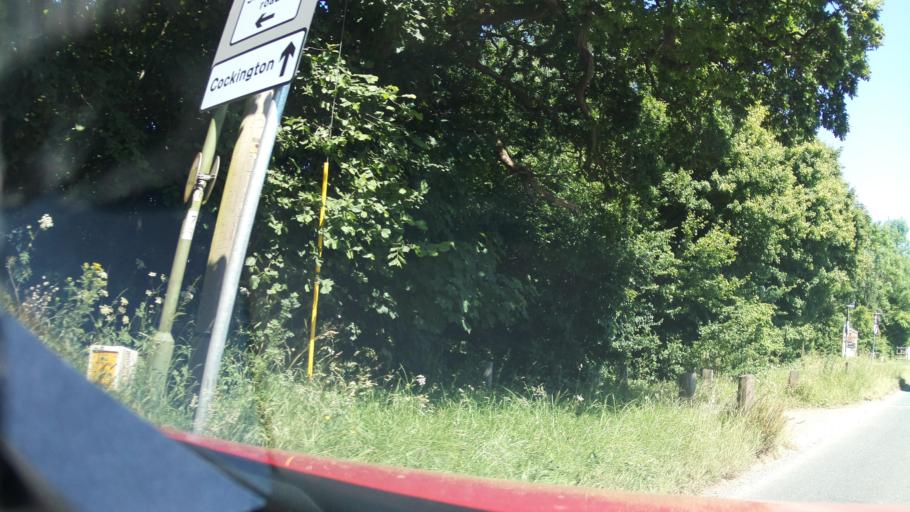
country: GB
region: England
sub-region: Devon
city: Marldon
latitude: 50.4570
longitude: -3.5869
